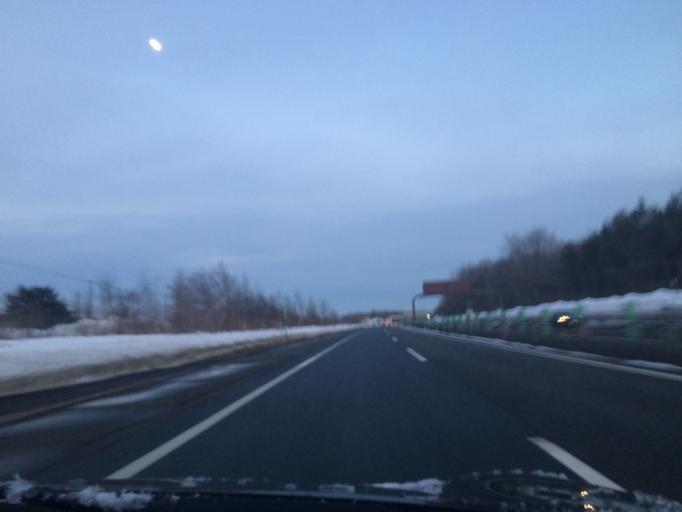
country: JP
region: Hokkaido
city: Chitose
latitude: 42.8420
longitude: 141.5953
